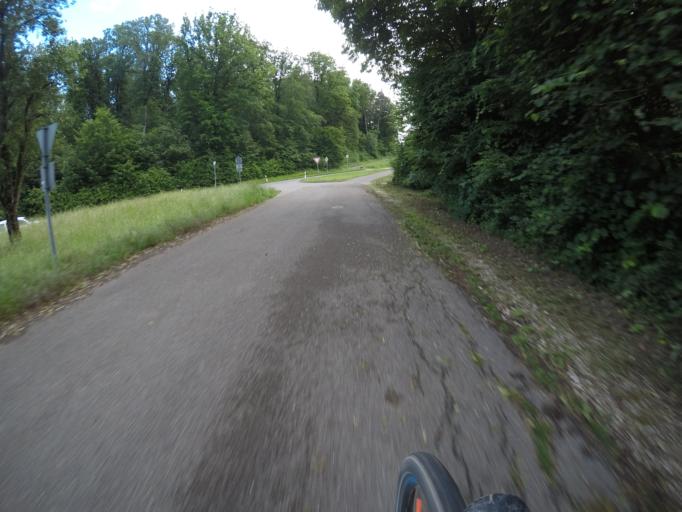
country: DE
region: Baden-Wuerttemberg
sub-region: Regierungsbezirk Stuttgart
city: Kohlberg
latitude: 48.5698
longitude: 9.3283
